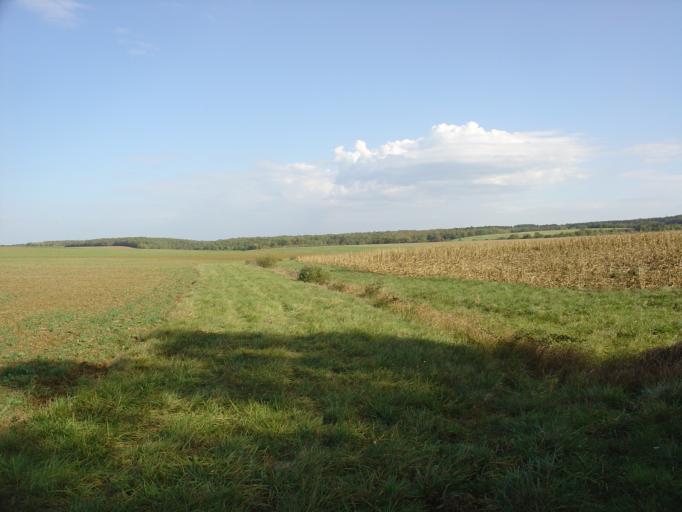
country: FR
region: Lorraine
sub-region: Departement de Meurthe-et-Moselle
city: Colombey-les-Belles
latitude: 48.5548
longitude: 5.9038
